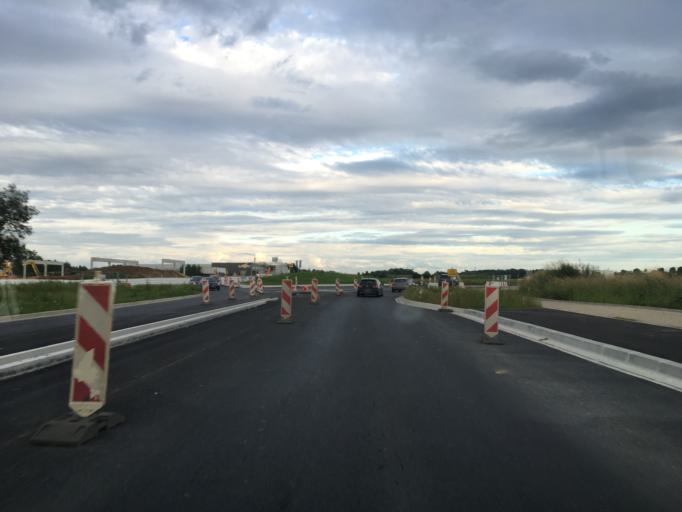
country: FR
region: Ile-de-France
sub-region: Departement de Seine-et-Marne
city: Servon
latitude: 48.7096
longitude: 2.5846
